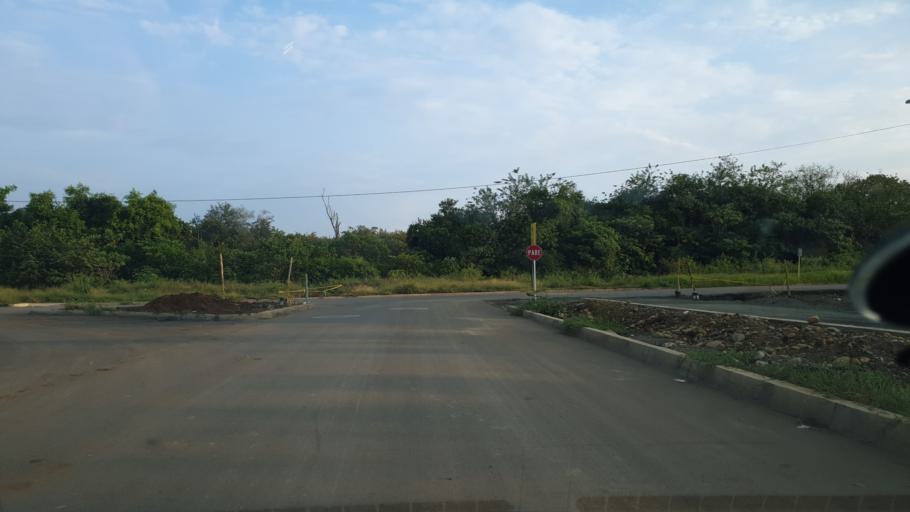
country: CO
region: Valle del Cauca
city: Jamundi
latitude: 3.3435
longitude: -76.5205
